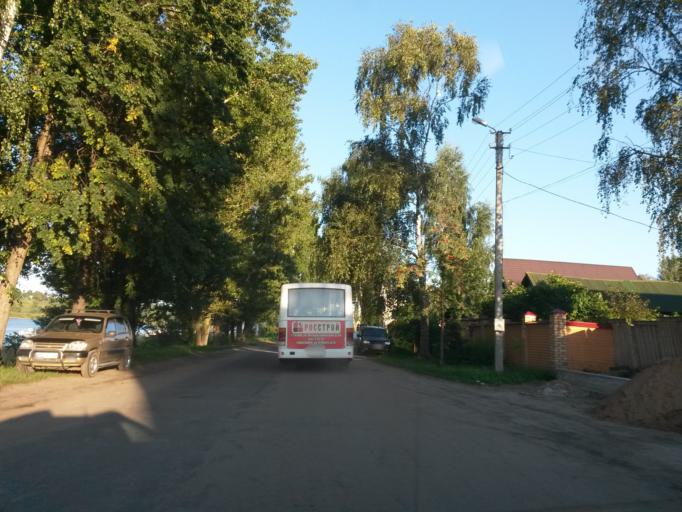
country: RU
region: Jaroslavl
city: Tutayev
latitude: 57.8732
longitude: 39.5363
